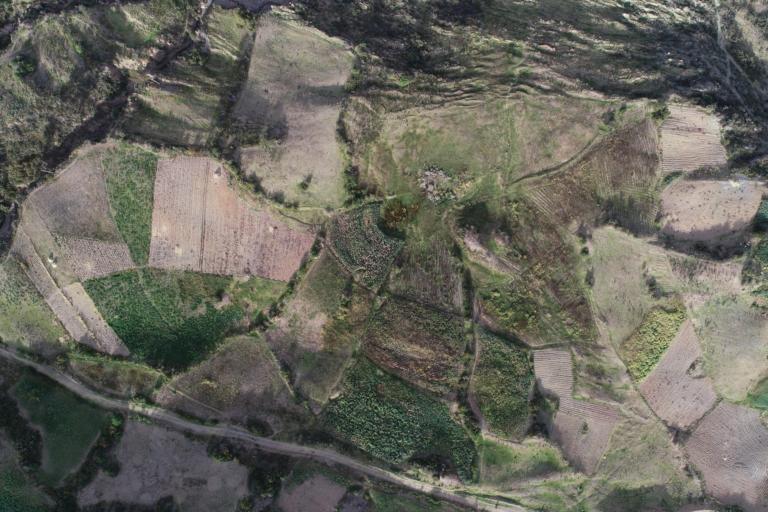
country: BO
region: La Paz
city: La Paz
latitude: -16.5488
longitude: -67.9967
